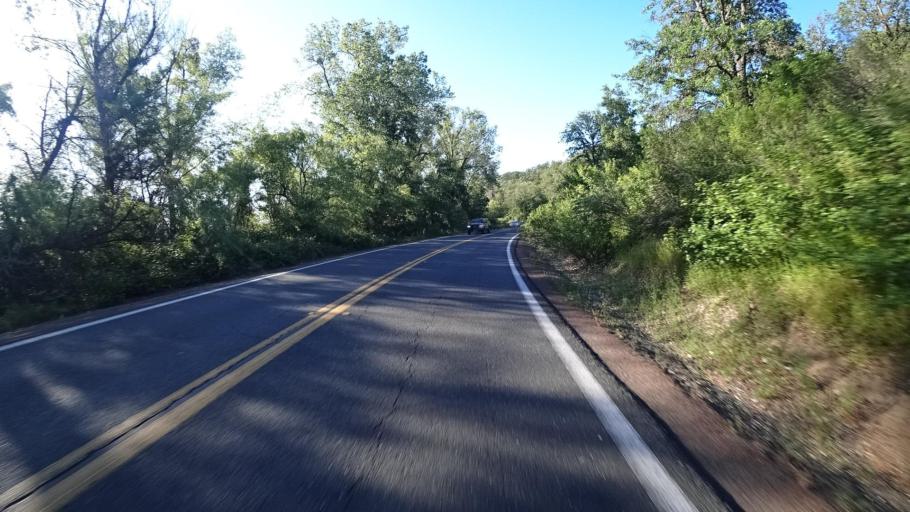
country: US
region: California
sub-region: Lake County
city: North Lakeport
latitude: 39.1202
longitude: -122.8898
